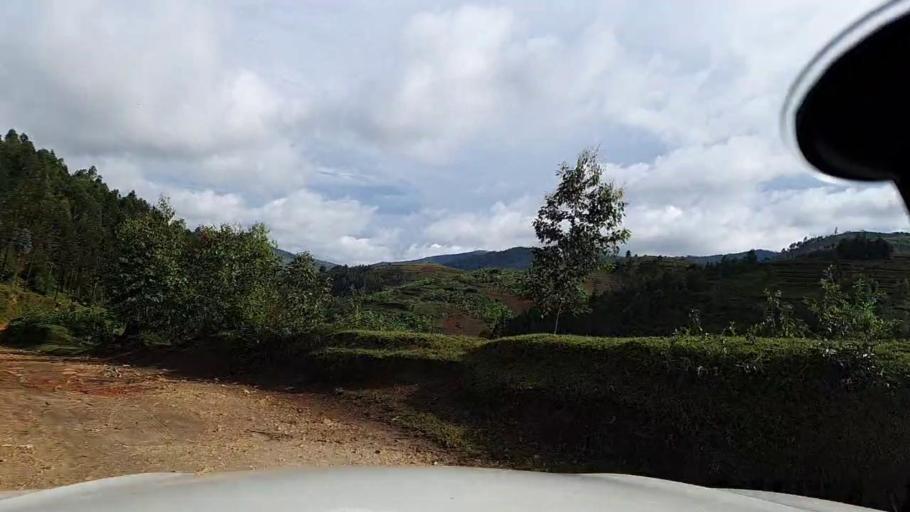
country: RW
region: Western Province
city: Kibuye
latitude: -2.1257
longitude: 29.4976
